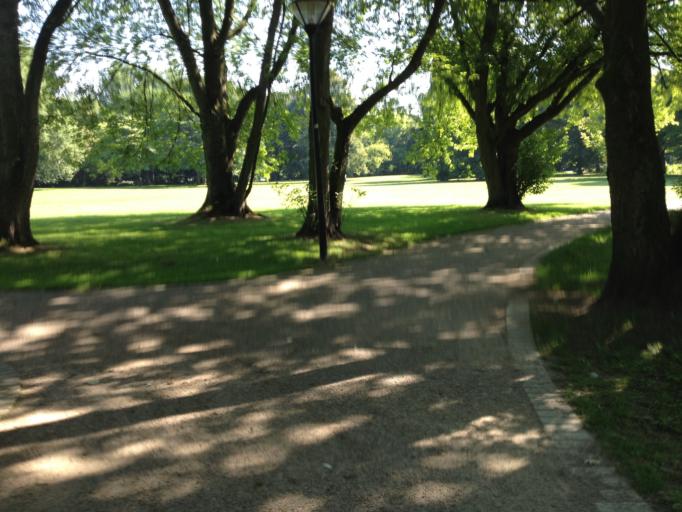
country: DE
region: North Rhine-Westphalia
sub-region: Regierungsbezirk Detmold
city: Guetersloh
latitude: 51.9021
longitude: 8.3894
